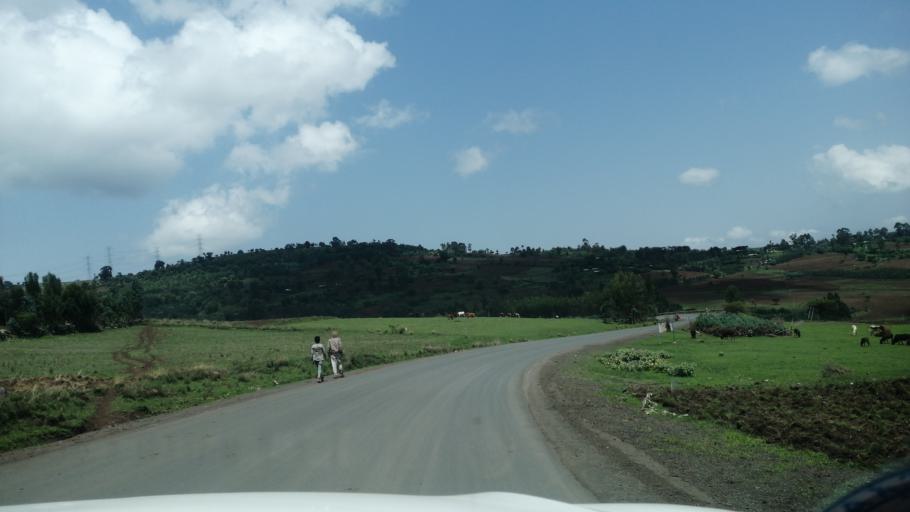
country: ET
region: Oromiya
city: Gedo
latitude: 8.9687
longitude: 37.5823
